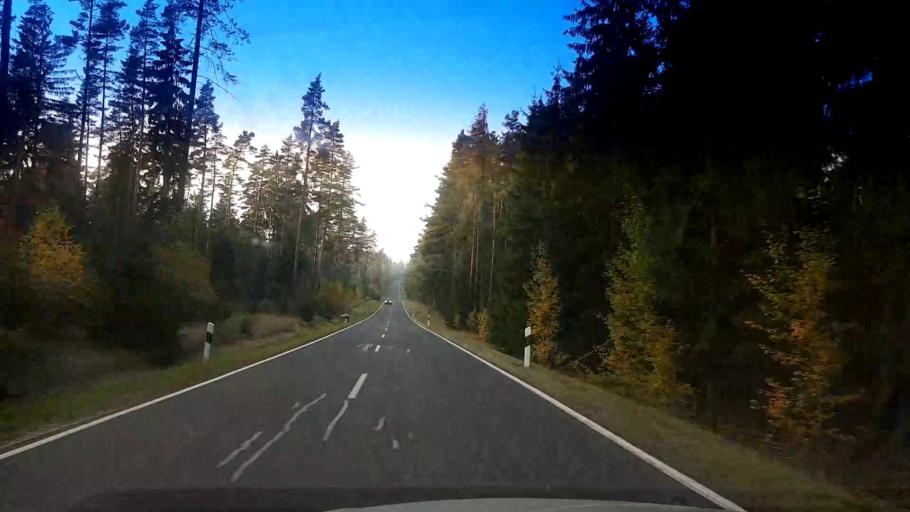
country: DE
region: Bavaria
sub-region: Upper Franconia
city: Schirnding
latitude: 50.0655
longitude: 12.2484
